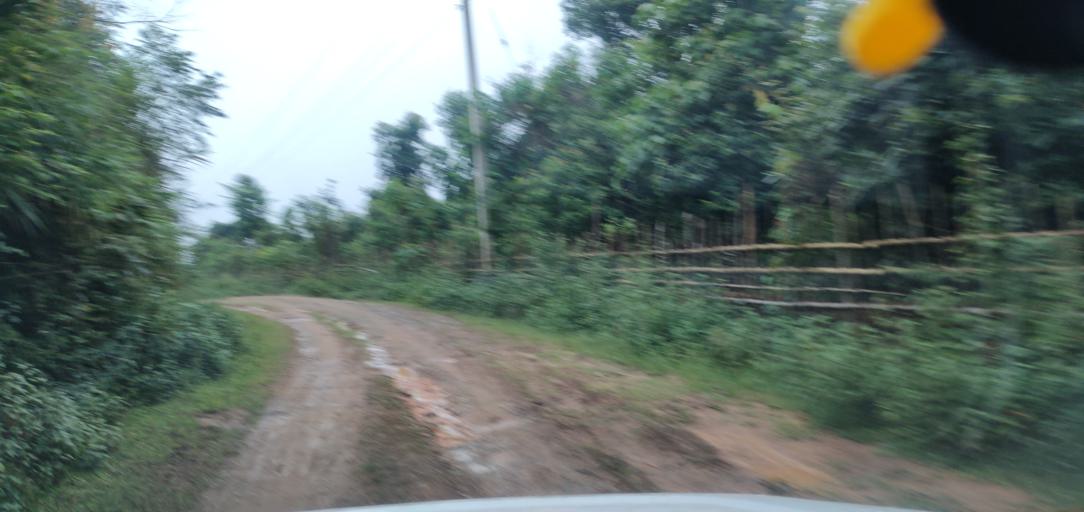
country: LA
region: Phongsali
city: Phongsali
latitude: 21.4304
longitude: 102.2616
